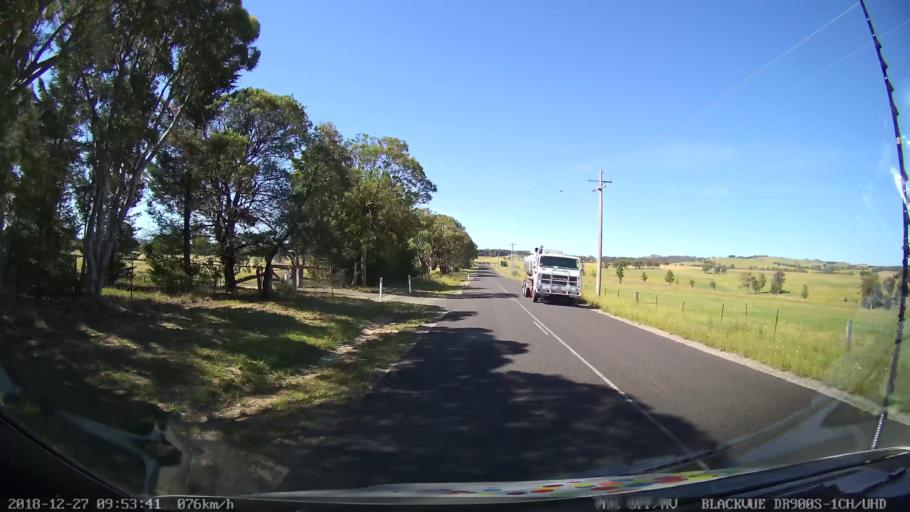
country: AU
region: New South Wales
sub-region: Lithgow
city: Portland
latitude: -33.3849
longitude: 149.9867
